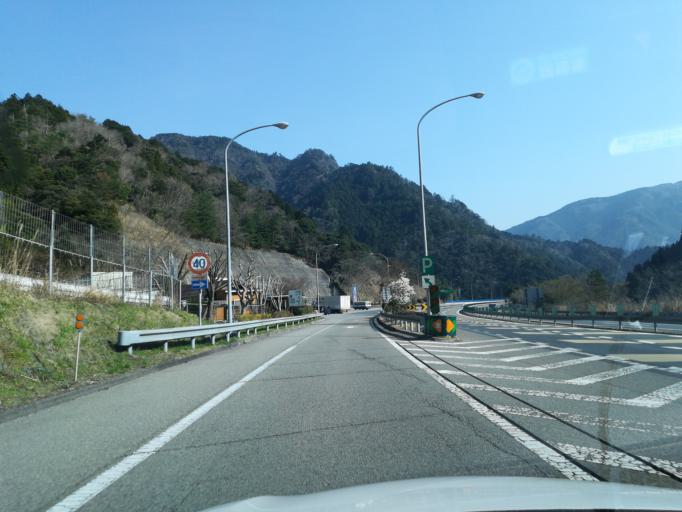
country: JP
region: Ehime
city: Kawanoecho
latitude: 33.9099
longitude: 133.6301
